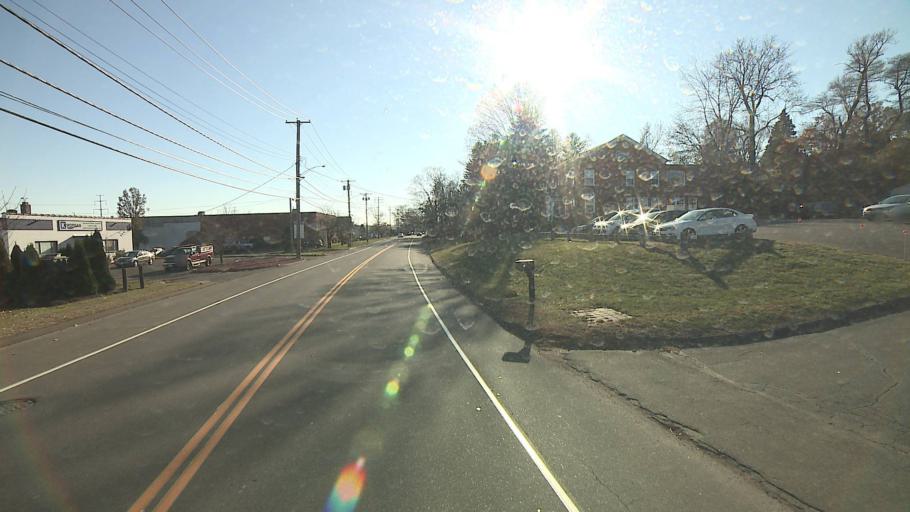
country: US
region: Connecticut
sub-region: New Haven County
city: Hamden
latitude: 41.3625
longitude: -72.8877
